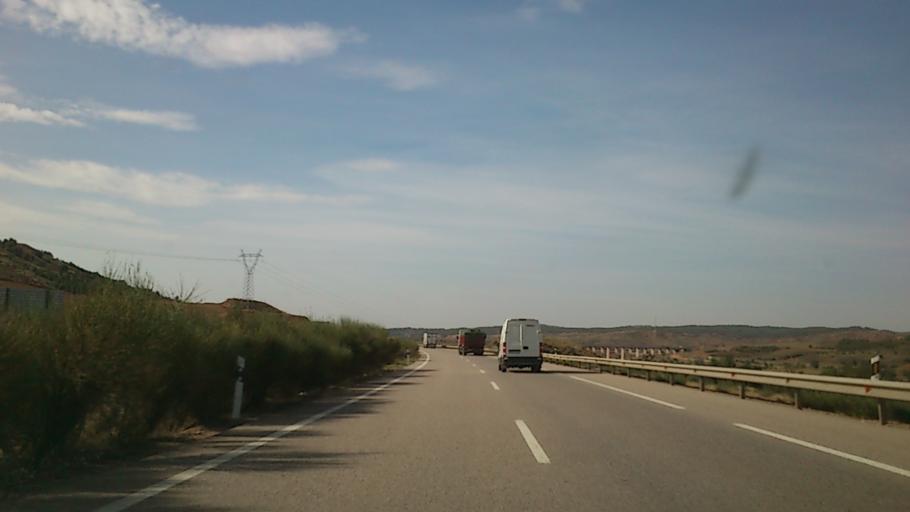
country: ES
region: Aragon
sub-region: Provincia de Teruel
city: Calamocha
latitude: 40.9340
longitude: -1.2683
